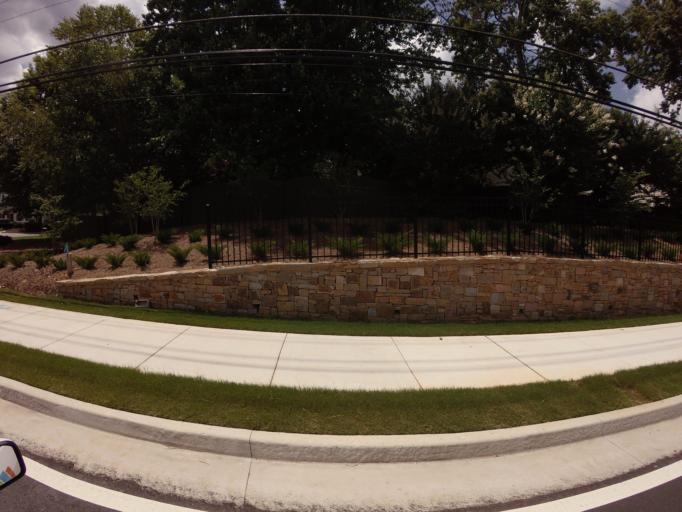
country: US
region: Georgia
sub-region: Fulton County
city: Johns Creek
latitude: 34.0605
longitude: -84.2161
